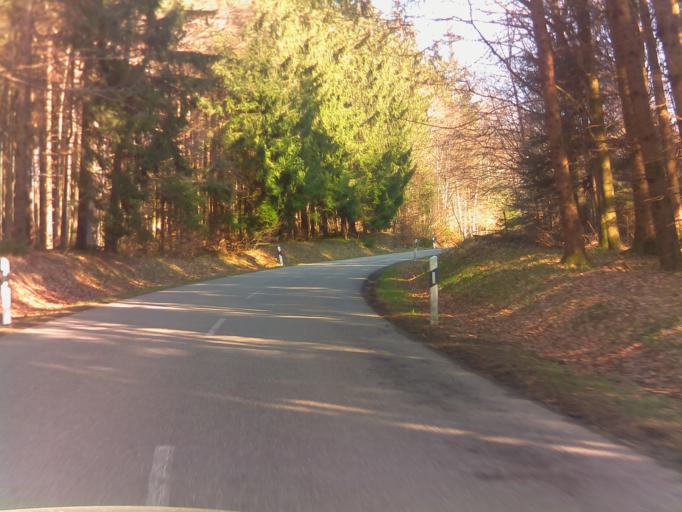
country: DE
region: Bavaria
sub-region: Swabia
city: Waltenhausen
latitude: 48.1661
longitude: 10.3778
